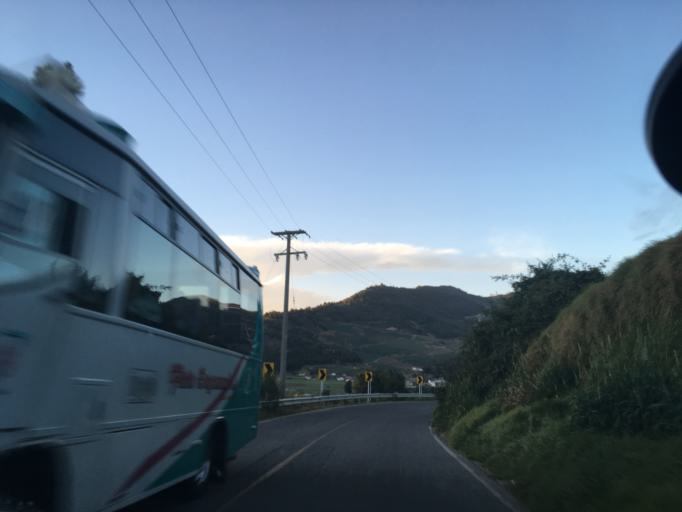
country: CO
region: Boyaca
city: Aquitania
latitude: 5.5779
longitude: -72.8934
